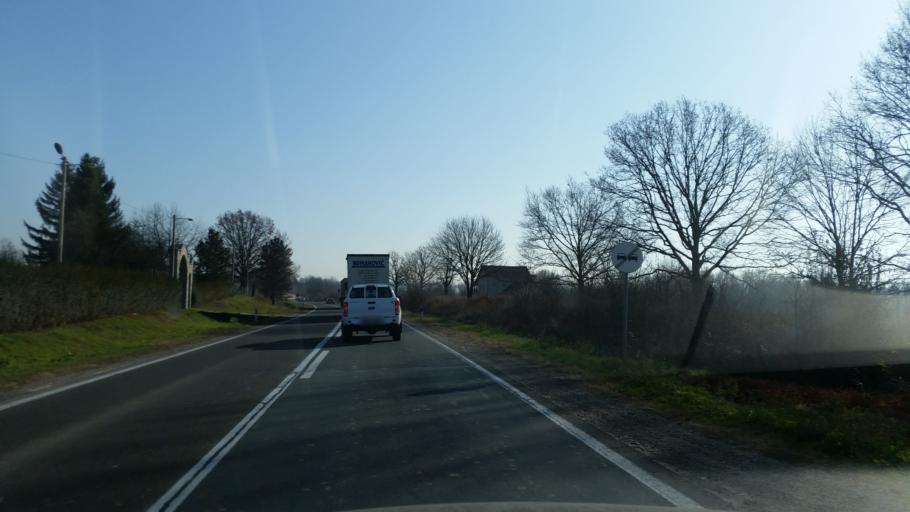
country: RS
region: Central Serbia
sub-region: Belgrade
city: Lazarevac
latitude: 44.3087
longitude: 20.2472
